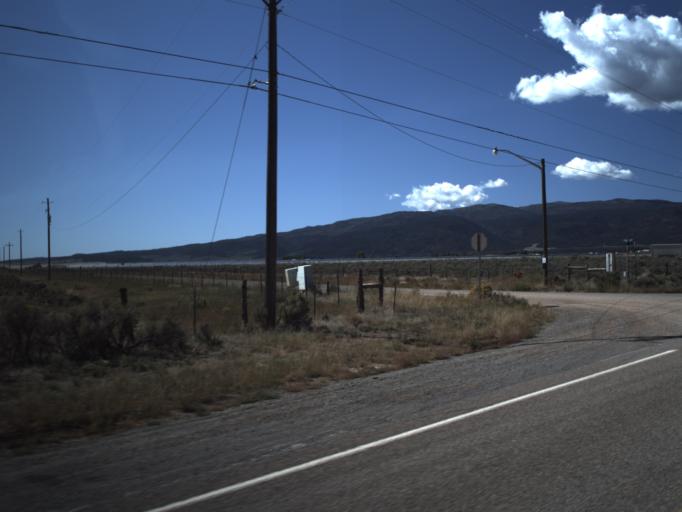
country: US
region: Utah
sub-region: Iron County
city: Cedar City
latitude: 37.6588
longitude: -113.2162
